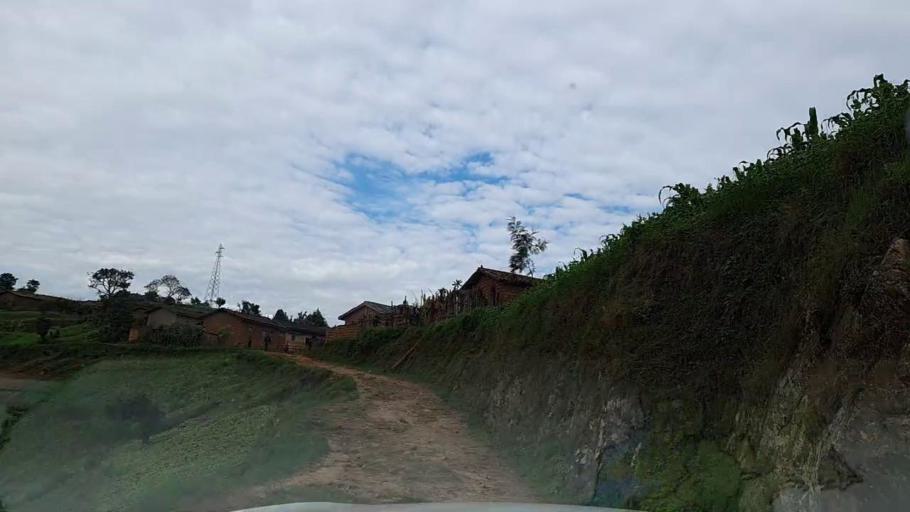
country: RW
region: Southern Province
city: Nzega
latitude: -2.4087
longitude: 29.4936
